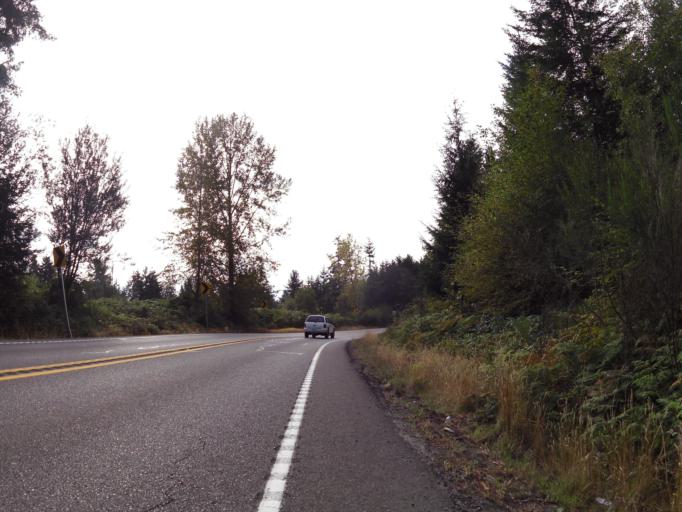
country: US
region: Washington
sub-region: Mason County
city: Allyn
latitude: 47.4096
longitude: -122.8399
